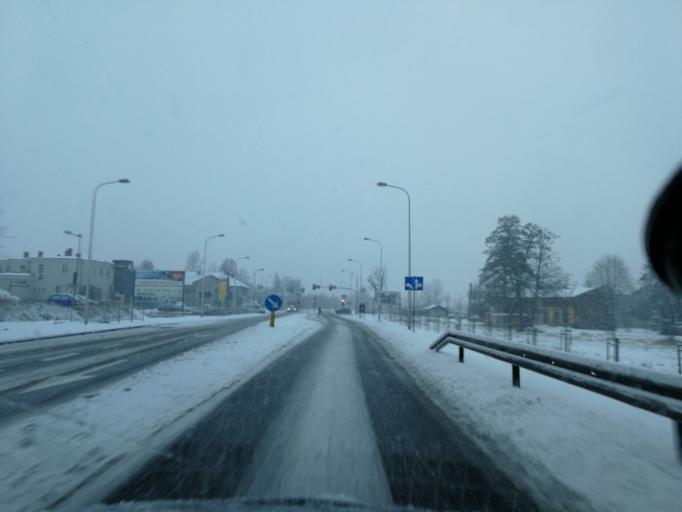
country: PL
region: Silesian Voivodeship
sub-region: Zory
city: Zory
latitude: 50.0478
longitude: 18.7028
